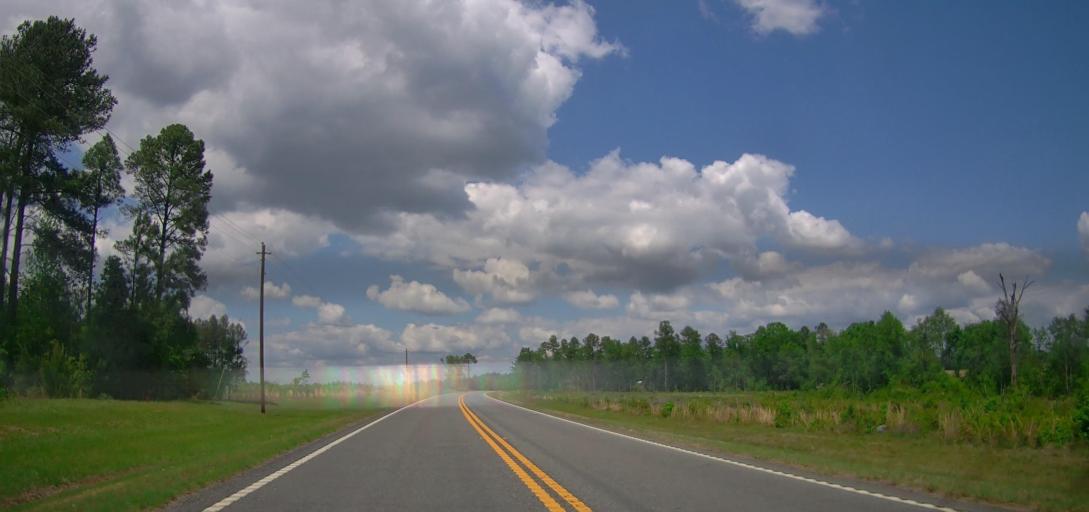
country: US
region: Georgia
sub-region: Treutlen County
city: Soperton
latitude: 32.4107
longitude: -82.6080
